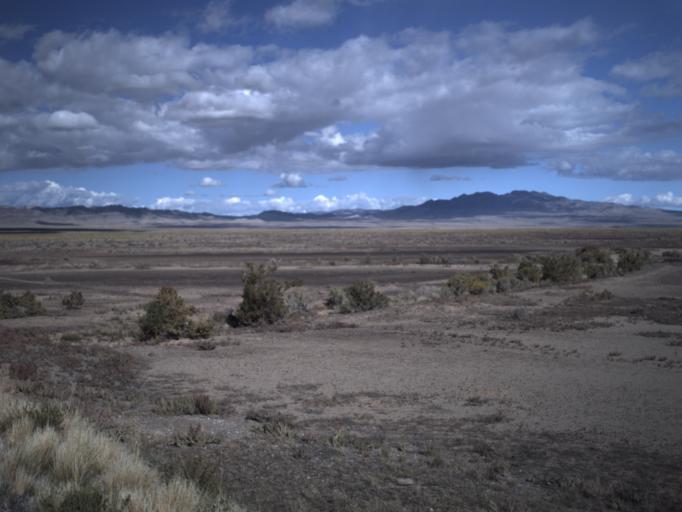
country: US
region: Utah
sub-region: Beaver County
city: Milford
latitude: 38.5321
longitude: -113.6811
